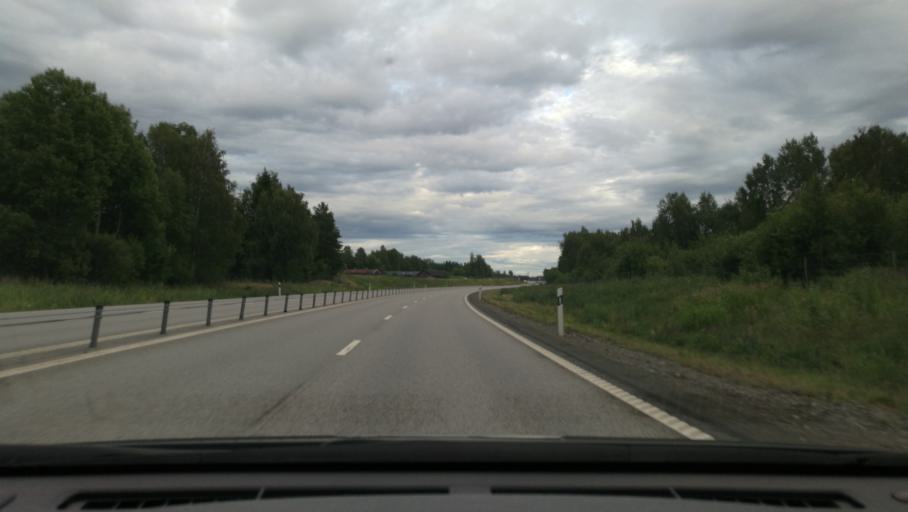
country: SE
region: OEstergoetland
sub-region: Norrkopings Kommun
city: Svartinge
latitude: 58.6440
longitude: 16.0808
